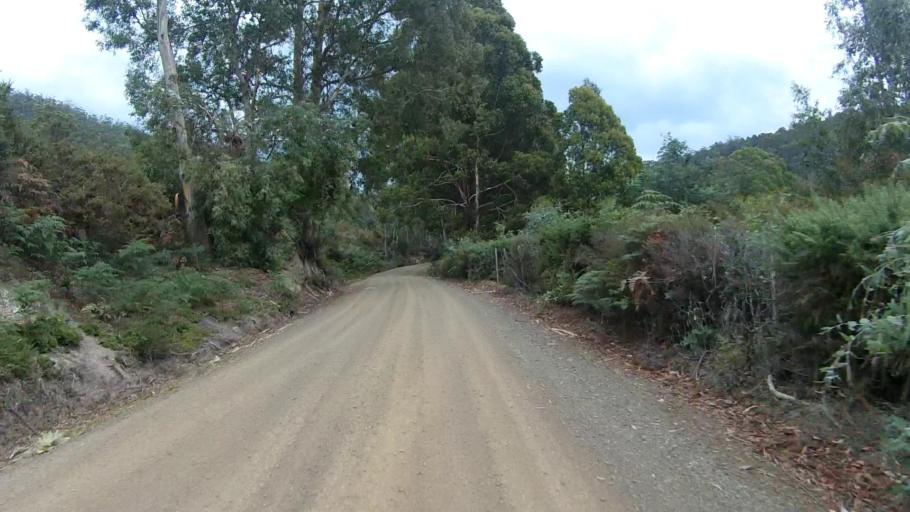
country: AU
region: Tasmania
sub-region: Kingborough
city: Kettering
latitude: -43.2224
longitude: 147.1752
